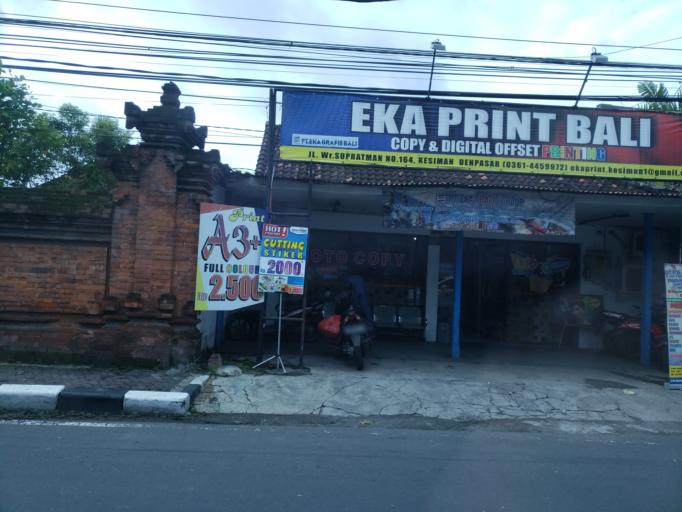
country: ID
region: Bali
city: Dajan Tangluk
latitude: -8.6481
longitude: 115.2394
